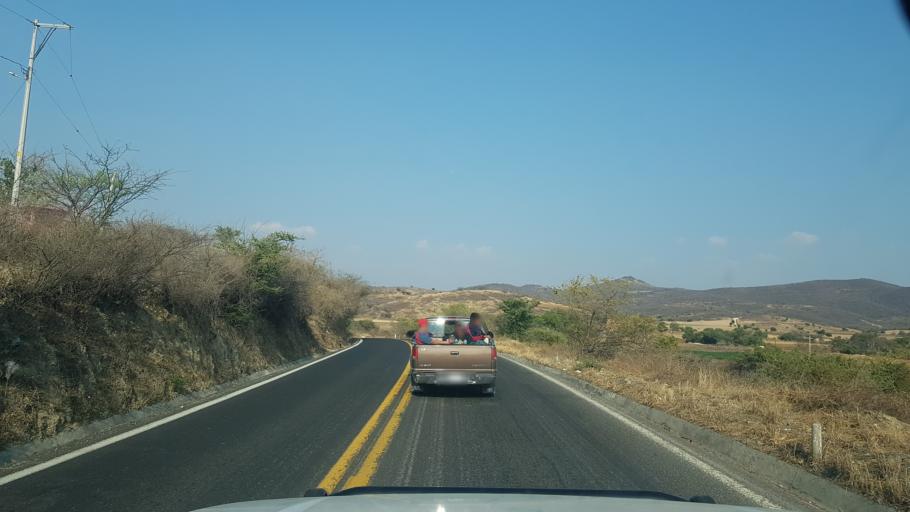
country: MX
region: Puebla
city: Calmeca
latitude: 18.6430
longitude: -98.6255
